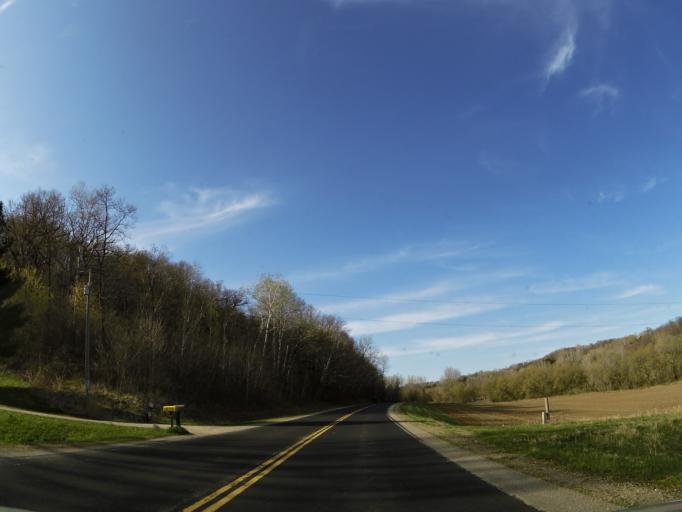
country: US
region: Minnesota
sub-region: Goodhue County
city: Red Wing
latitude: 44.6623
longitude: -92.6123
